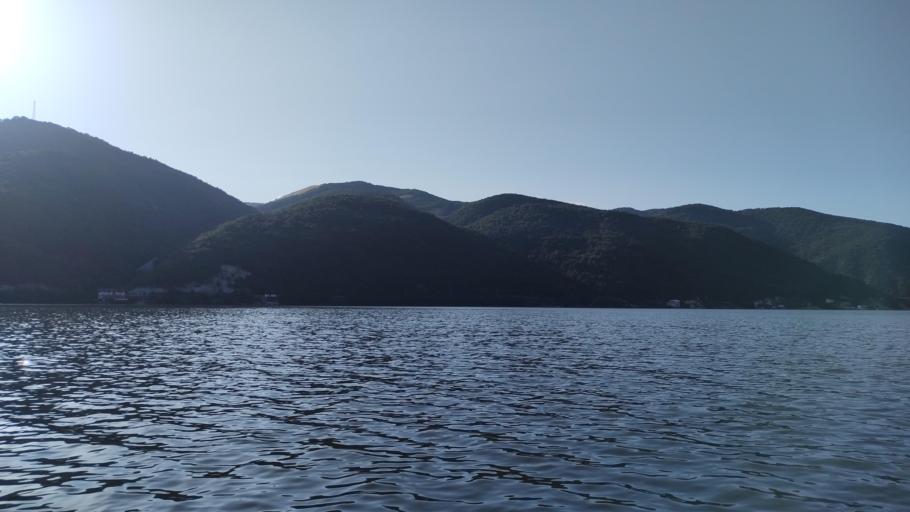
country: RO
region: Mehedinti
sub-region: Comuna Dubova
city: Dubova
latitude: 44.5562
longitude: 22.2307
